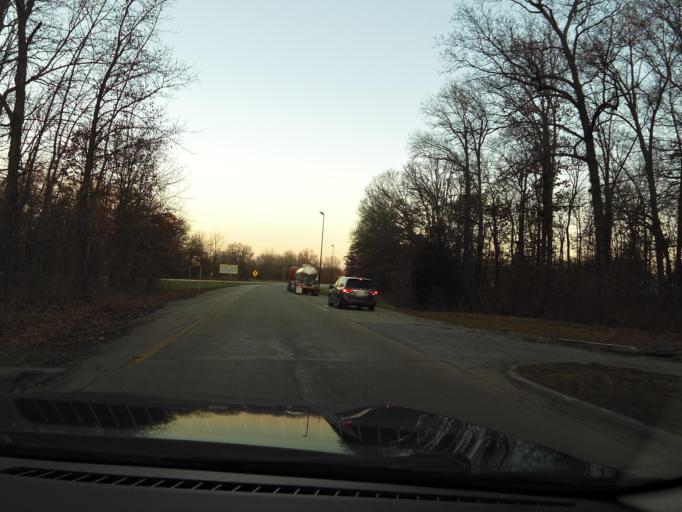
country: US
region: Illinois
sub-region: Marion County
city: Salem
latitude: 38.5975
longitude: -88.9646
